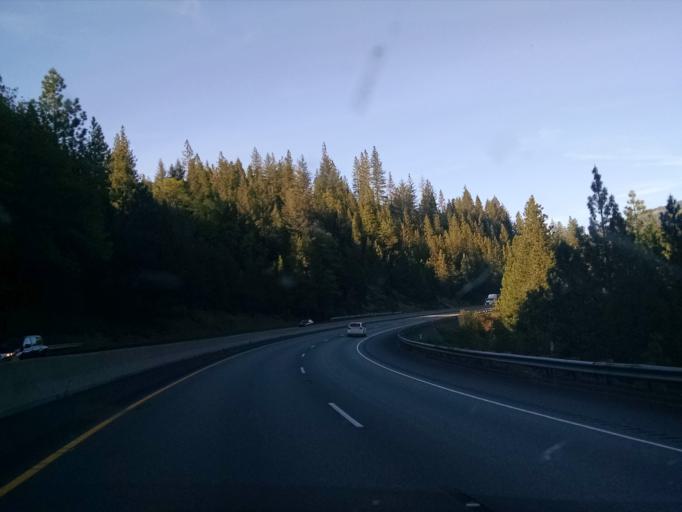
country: US
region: California
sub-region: Siskiyou County
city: Dunsmuir
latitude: 41.0902
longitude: -122.3527
